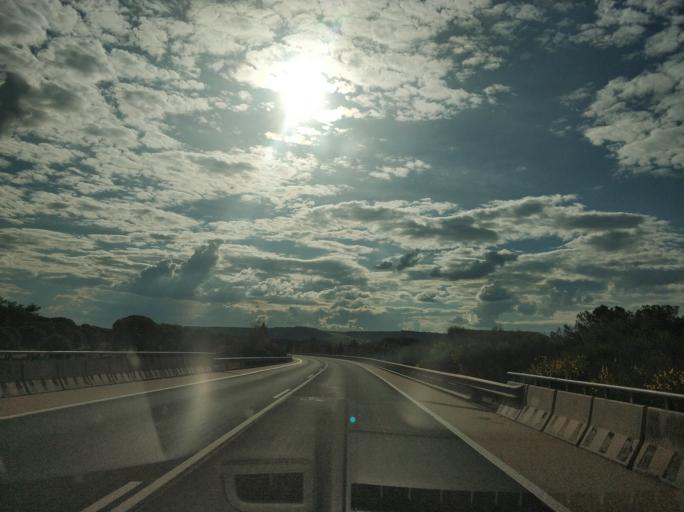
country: ES
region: Castille and Leon
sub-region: Provincia de Valladolid
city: Quintanilla de Onesimo
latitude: 41.6213
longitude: -4.3768
